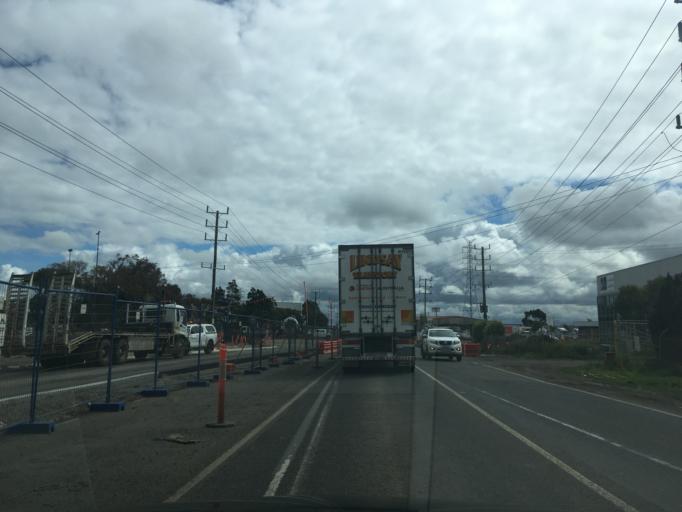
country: AU
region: Victoria
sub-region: Brimbank
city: Brooklyn
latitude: -37.8297
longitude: 144.8050
